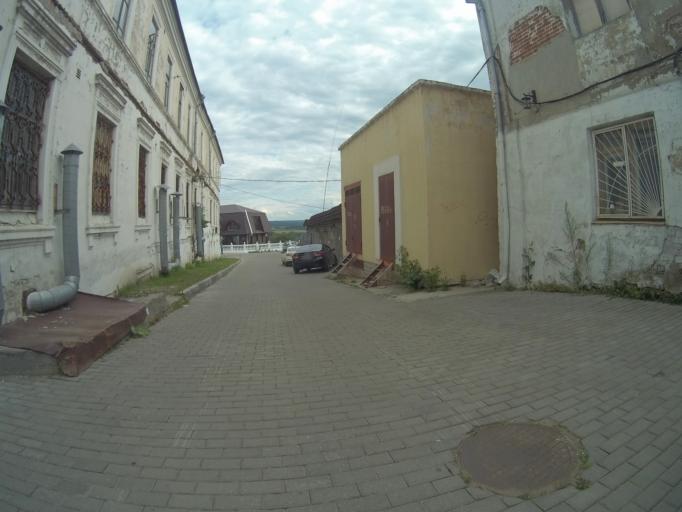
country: RU
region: Vladimir
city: Vladimir
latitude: 56.1280
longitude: 40.4050
